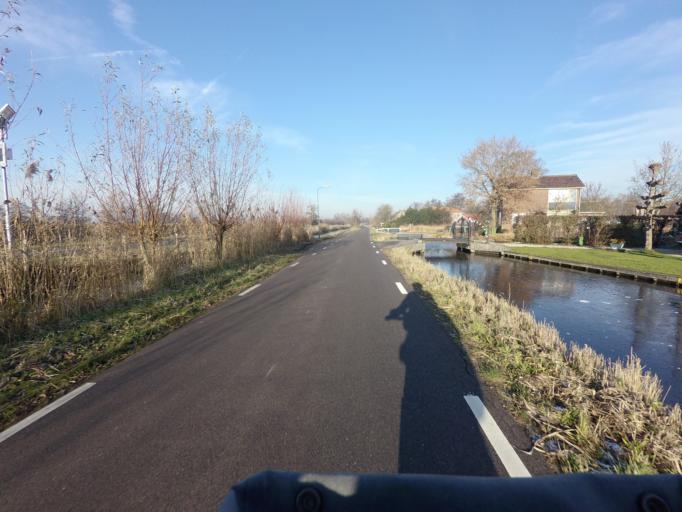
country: NL
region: Utrecht
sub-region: Gemeente De Ronde Venen
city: Mijdrecht
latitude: 52.1612
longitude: 4.8552
